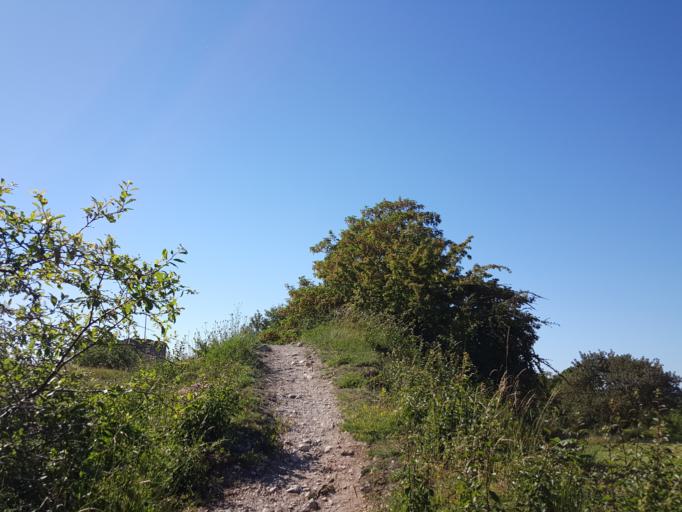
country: SE
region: Gotland
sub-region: Gotland
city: Visby
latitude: 57.6443
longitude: 18.3029
